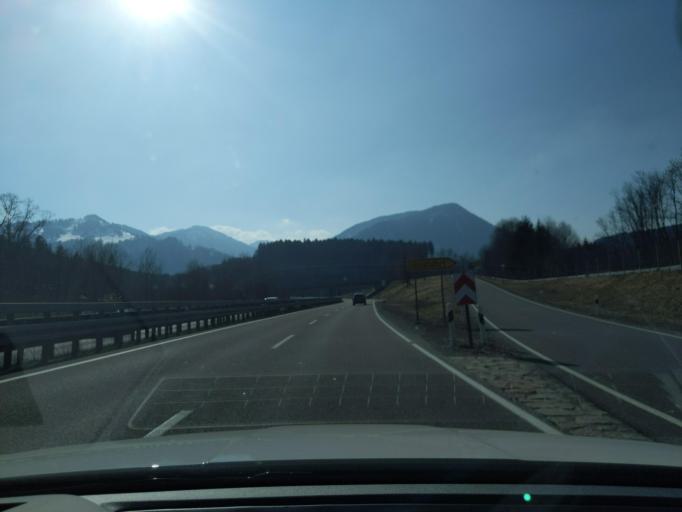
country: DE
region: Bavaria
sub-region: Swabia
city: Immenstadt im Allgau
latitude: 47.5722
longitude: 10.2461
